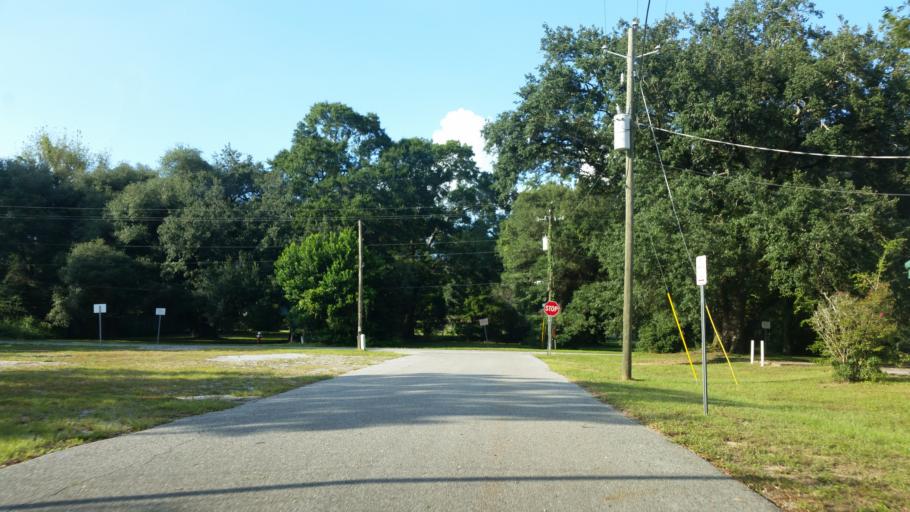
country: US
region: Florida
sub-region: Escambia County
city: Ferry Pass
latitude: 30.4828
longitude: -87.1941
